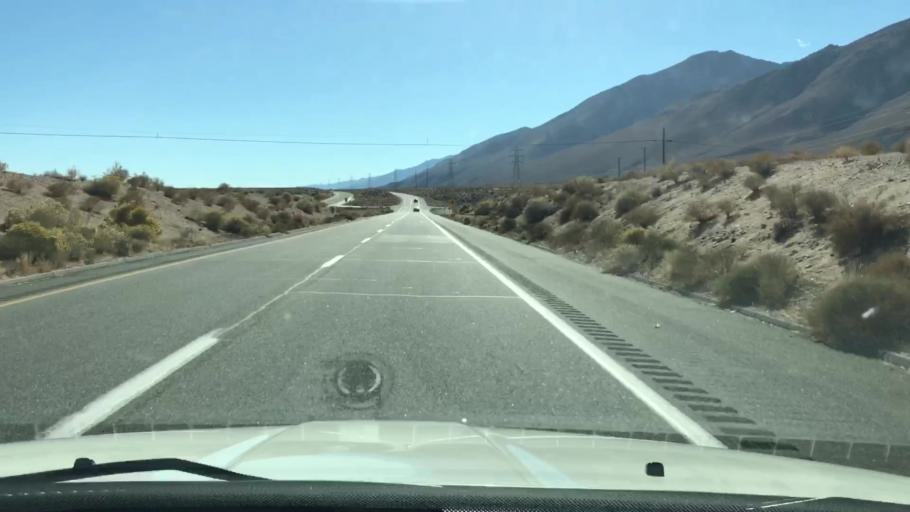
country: US
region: California
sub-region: Inyo County
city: Lone Pine
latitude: 36.4467
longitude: -118.0349
